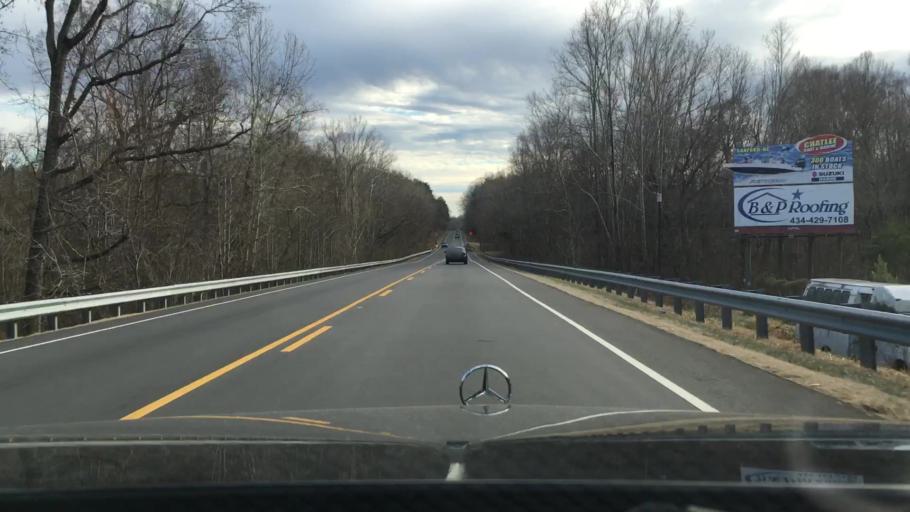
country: US
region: North Carolina
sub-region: Caswell County
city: Yanceyville
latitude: 36.4791
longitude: -79.3795
